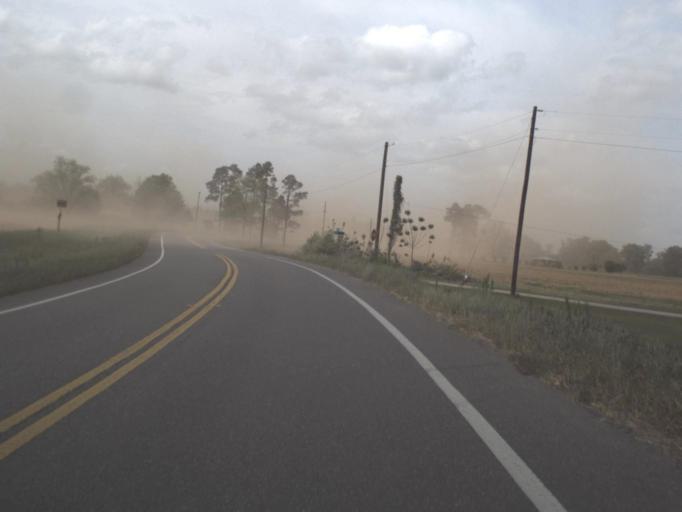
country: US
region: Alabama
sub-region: Escambia County
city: East Brewton
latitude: 30.9898
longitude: -87.1144
